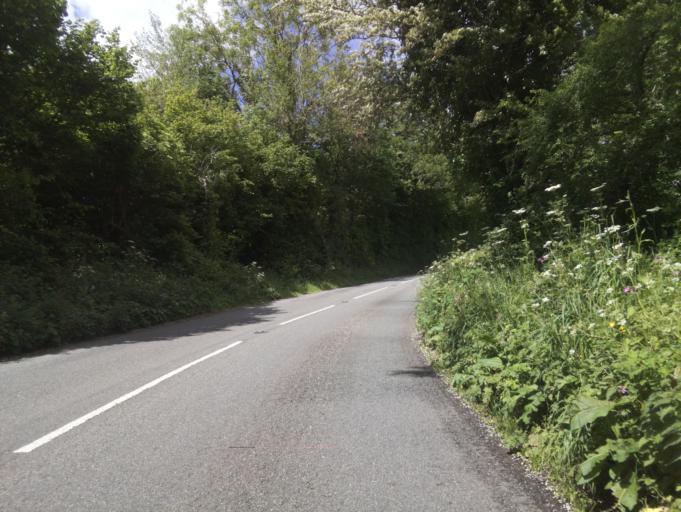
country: GB
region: England
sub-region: Devon
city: Dartmouth
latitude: 50.3622
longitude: -3.5616
